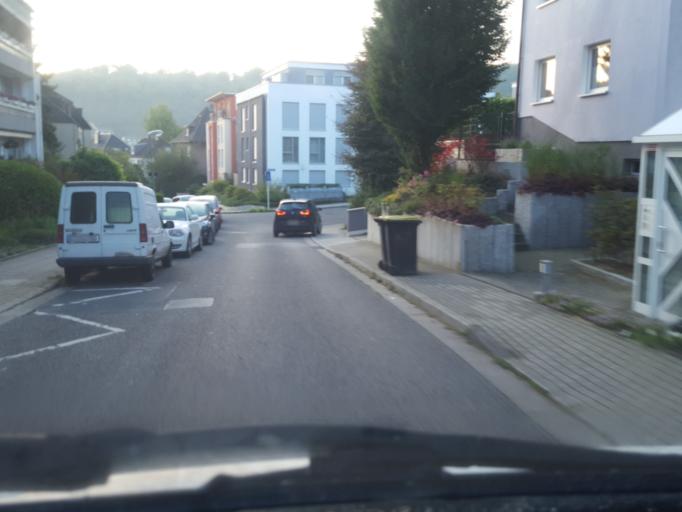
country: DE
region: North Rhine-Westphalia
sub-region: Regierungsbezirk Dusseldorf
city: Heiligenhaus
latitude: 51.3867
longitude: 6.9953
